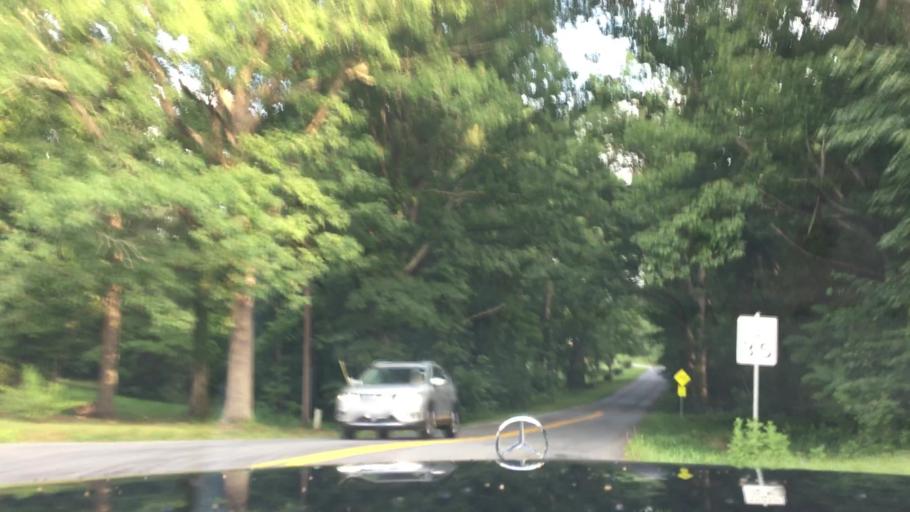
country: US
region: Virginia
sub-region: Campbell County
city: Timberlake
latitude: 37.2380
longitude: -79.2951
